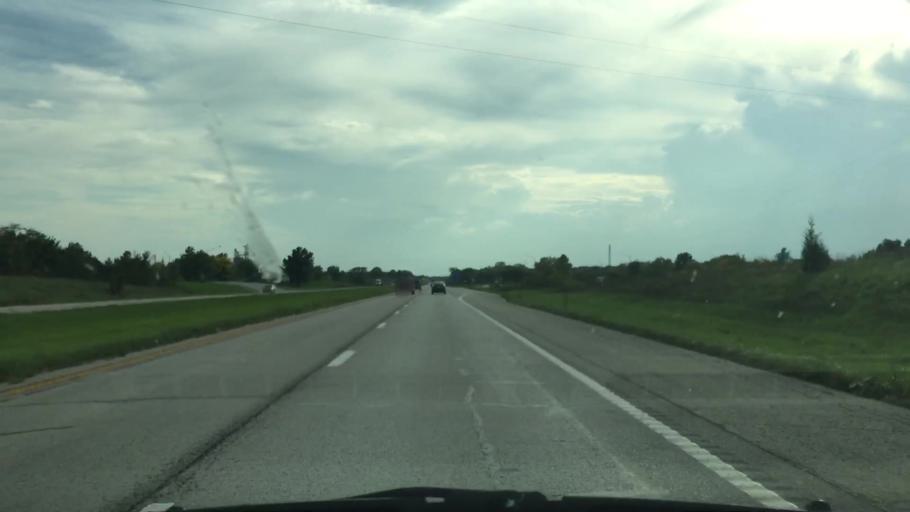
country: US
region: Missouri
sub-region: Harrison County
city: Bethany
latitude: 40.1199
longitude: -94.0592
